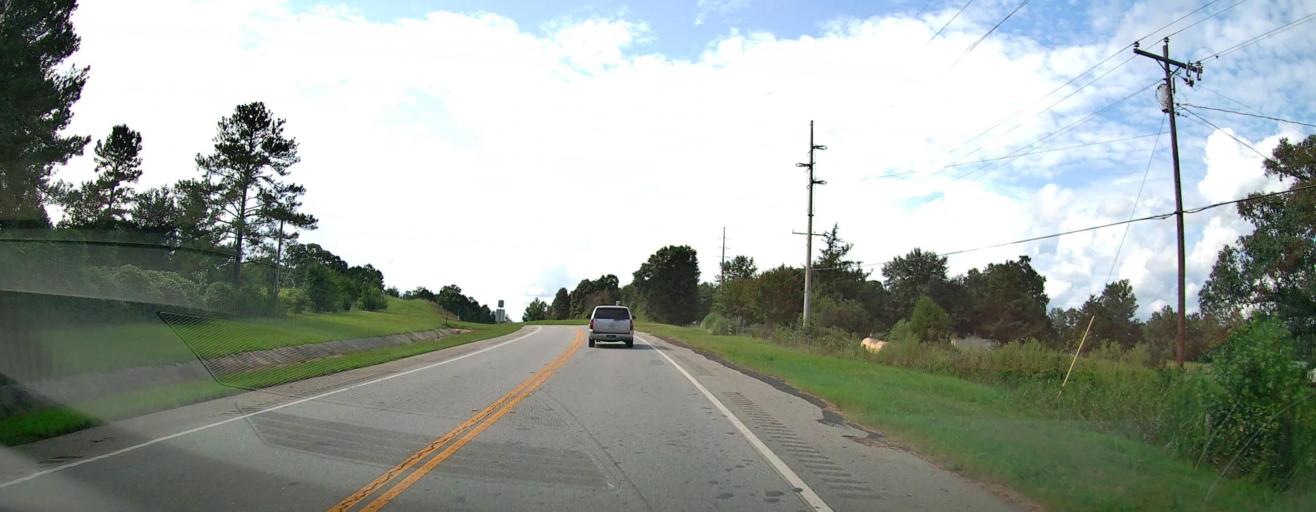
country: US
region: Georgia
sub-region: Upson County
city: Hannahs Mill
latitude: 32.9905
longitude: -84.5049
